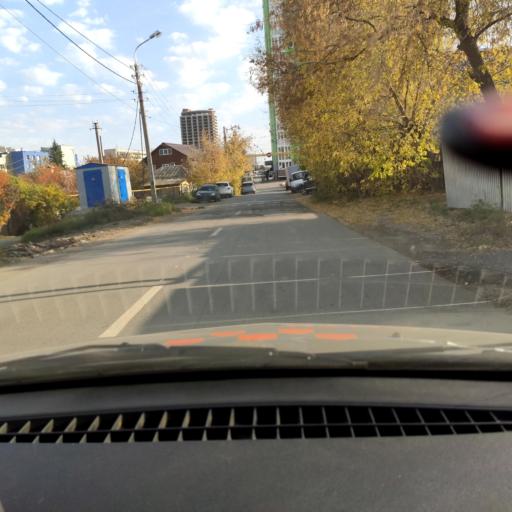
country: RU
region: Bashkortostan
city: Ufa
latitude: 54.7101
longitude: 55.9843
